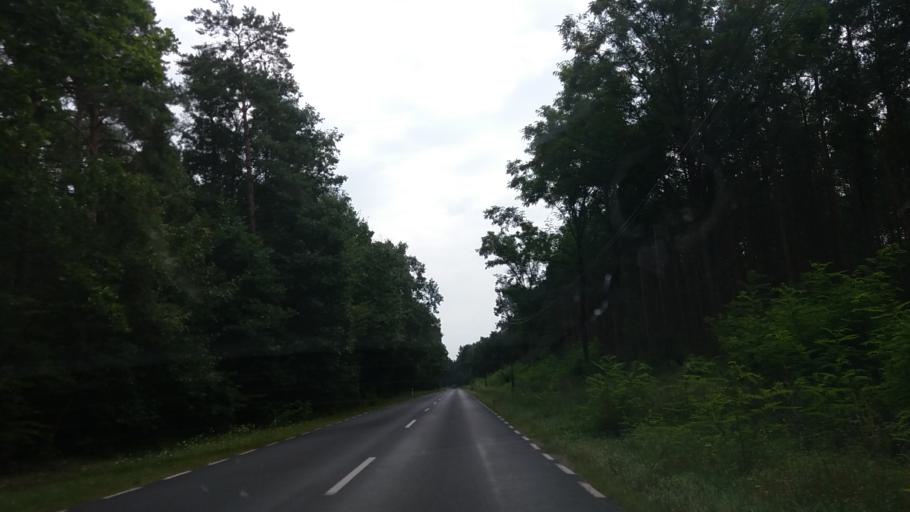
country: PL
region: Lubusz
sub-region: Powiat miedzyrzecki
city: Skwierzyna
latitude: 52.6377
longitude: 15.4545
